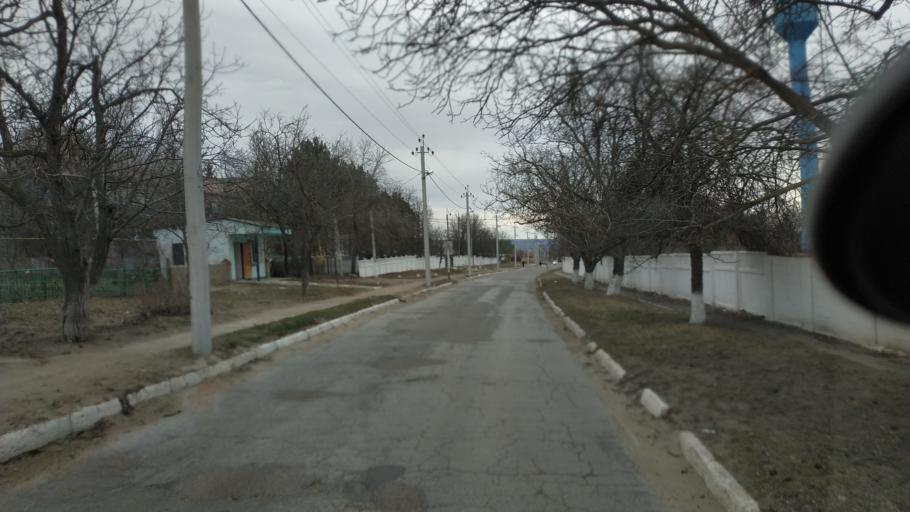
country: MD
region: Telenesti
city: Cocieri
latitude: 47.2941
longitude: 29.1187
